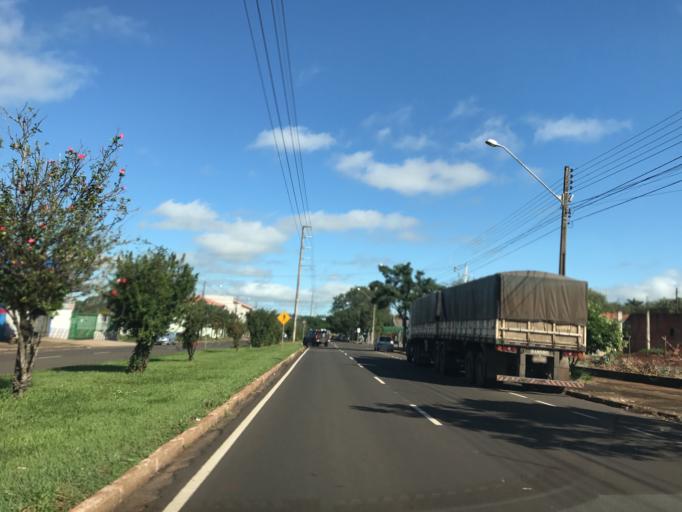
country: BR
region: Parana
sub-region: Maringa
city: Maringa
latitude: -23.4498
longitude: -51.9584
